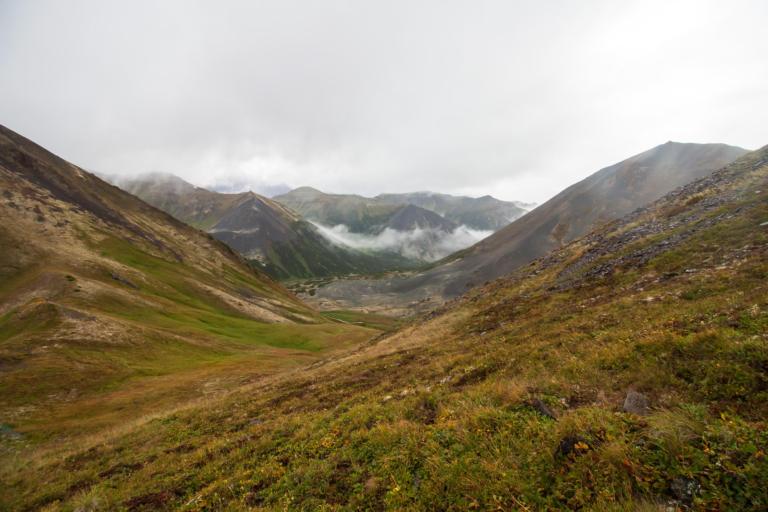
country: RU
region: Kamtsjatka
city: Yelizovo
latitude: 54.0067
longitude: 158.0911
